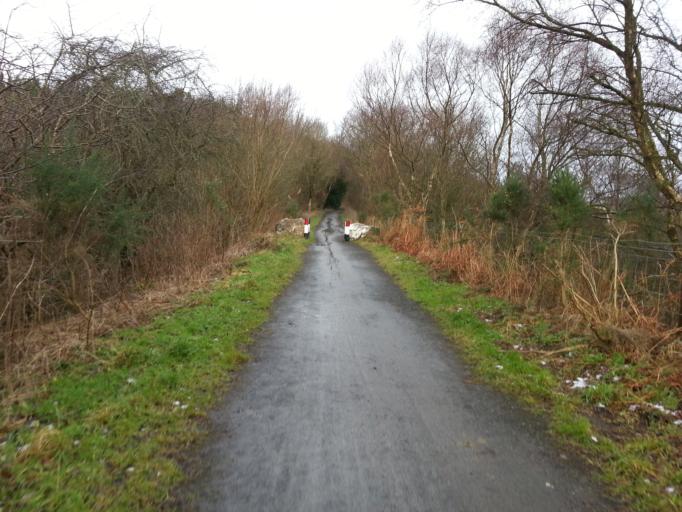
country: GB
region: England
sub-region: County Durham
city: Crook
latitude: 54.7476
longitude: -1.7347
